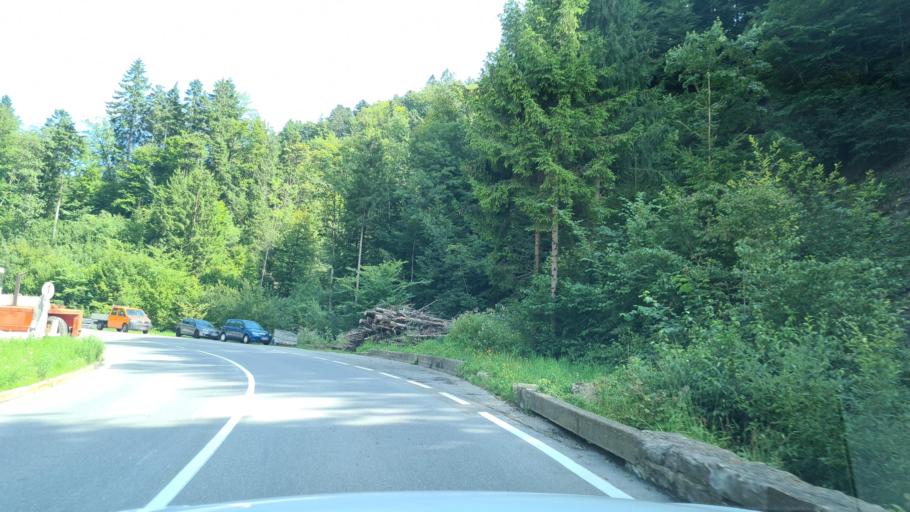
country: AT
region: Vorarlberg
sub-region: Politischer Bezirk Bregenz
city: Bildstein
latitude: 47.4429
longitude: 9.7866
